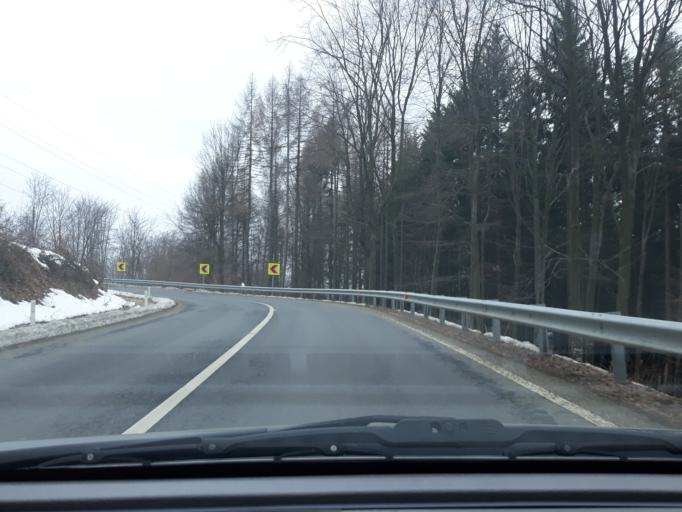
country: RO
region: Bihor
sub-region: Oras Alesd
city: Padurea Neagra
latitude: 47.1198
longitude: 22.4272
